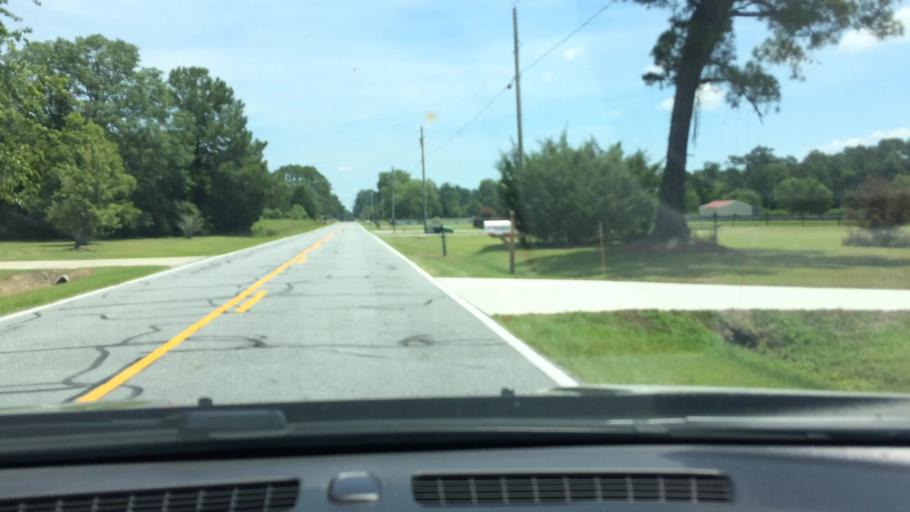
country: US
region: North Carolina
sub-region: Pitt County
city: Windsor
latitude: 35.4988
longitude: -77.3355
